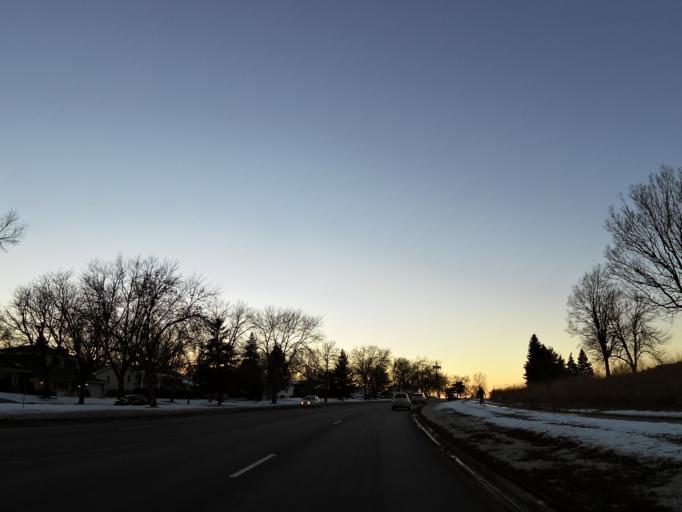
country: US
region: Minnesota
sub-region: Scott County
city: Savage
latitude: 44.8245
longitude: -93.3428
